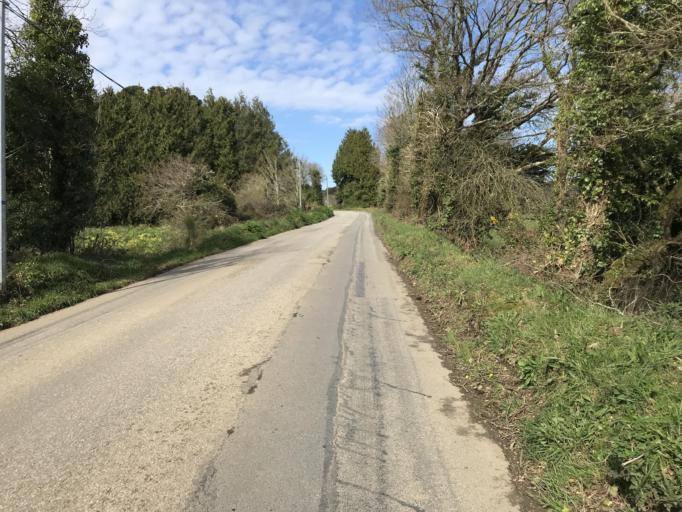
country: FR
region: Brittany
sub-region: Departement du Finistere
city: Daoulas
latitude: 48.3649
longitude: -4.2769
